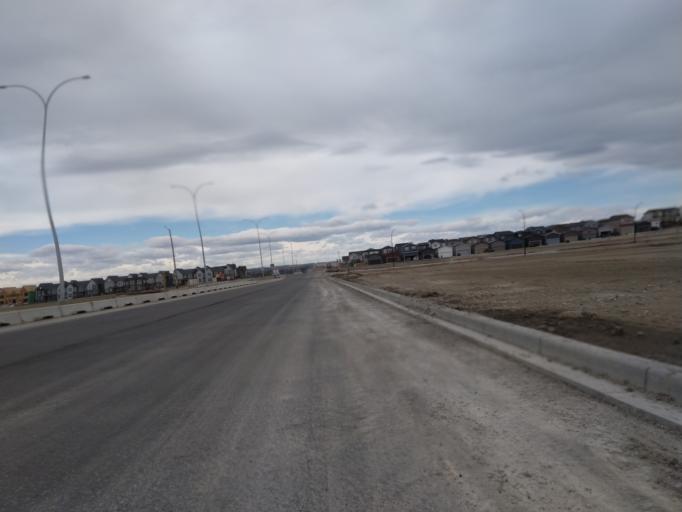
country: CA
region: Alberta
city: Airdrie
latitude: 51.1835
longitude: -114.0718
